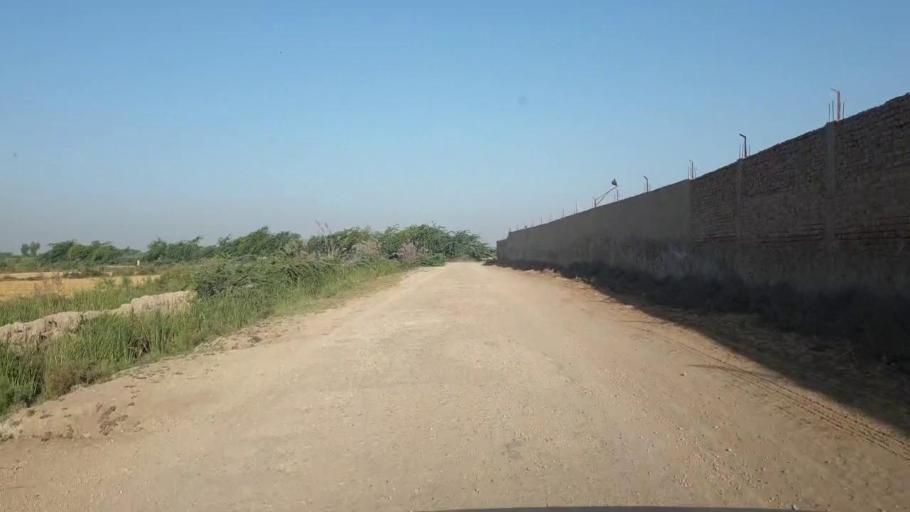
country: PK
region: Sindh
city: Badin
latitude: 24.6869
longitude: 68.8226
